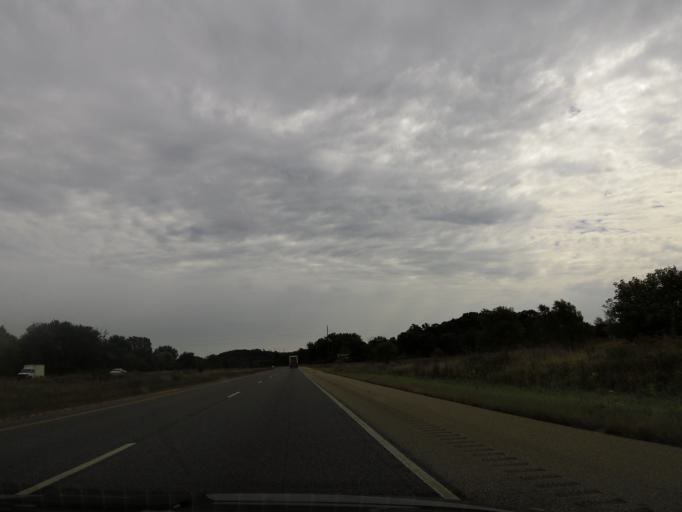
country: US
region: Wisconsin
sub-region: Monroe County
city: Tomah
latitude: 43.9467
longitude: -90.5553
